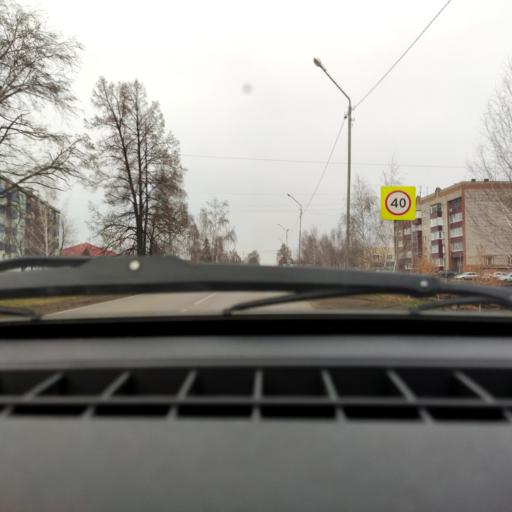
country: RU
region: Bashkortostan
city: Chishmy
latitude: 54.5888
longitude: 55.3941
